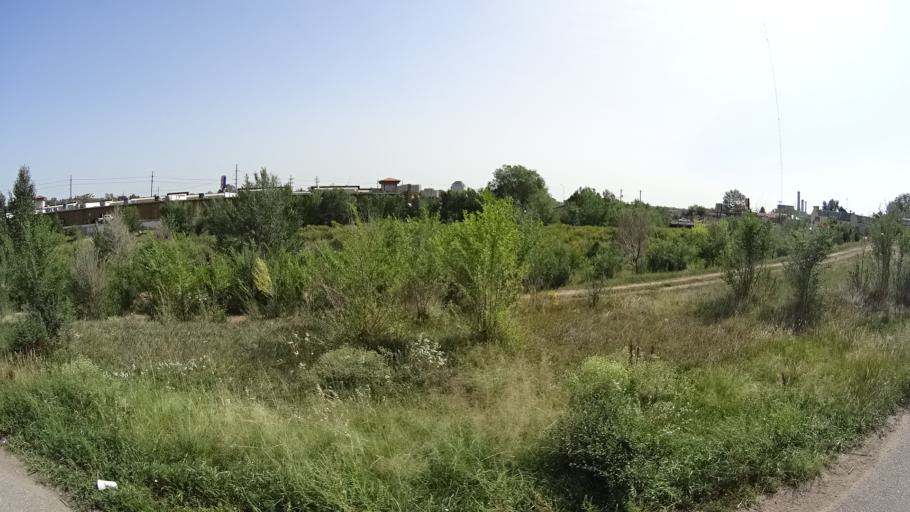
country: US
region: Colorado
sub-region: El Paso County
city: Colorado Springs
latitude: 38.8300
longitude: -104.8425
